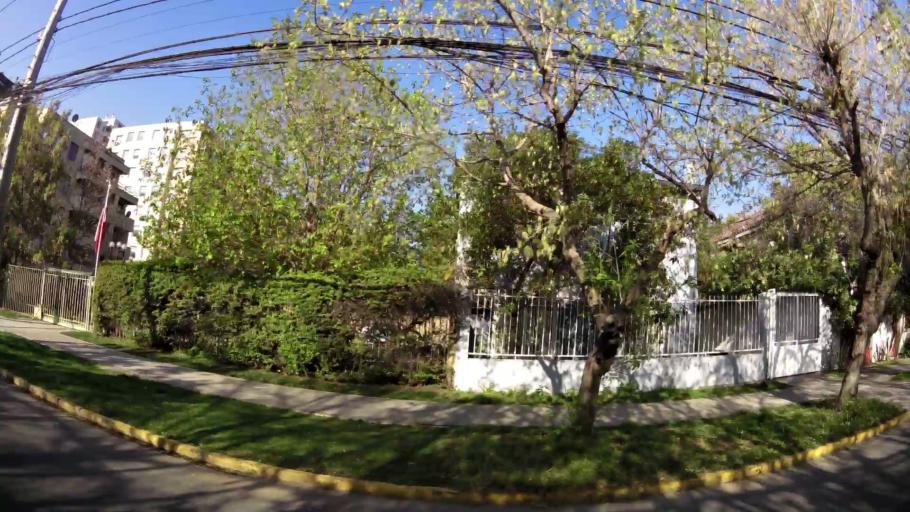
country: CL
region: Santiago Metropolitan
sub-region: Provincia de Santiago
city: Villa Presidente Frei, Nunoa, Santiago, Chile
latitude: -33.4539
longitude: -70.5962
